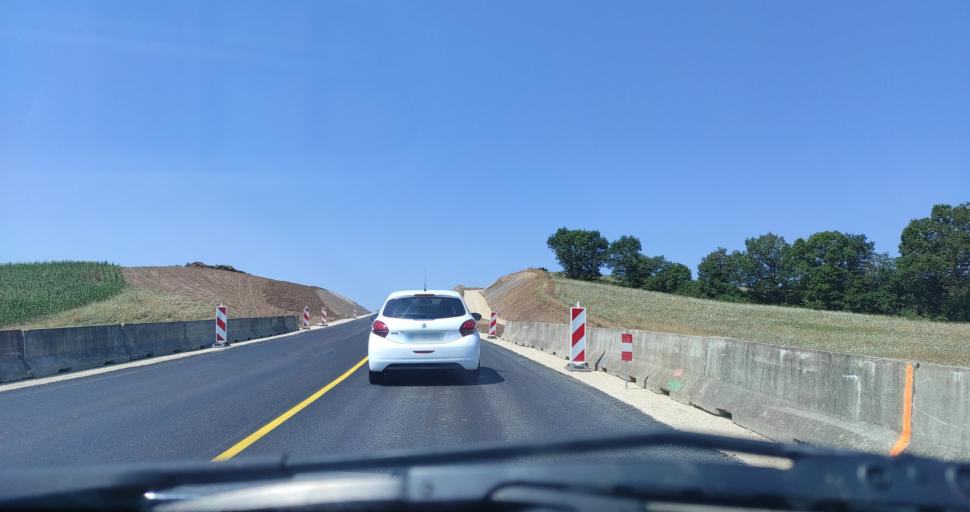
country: FR
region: Midi-Pyrenees
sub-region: Departement de l'Aveyron
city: Severac-le-Chateau
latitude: 44.2400
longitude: 2.9644
